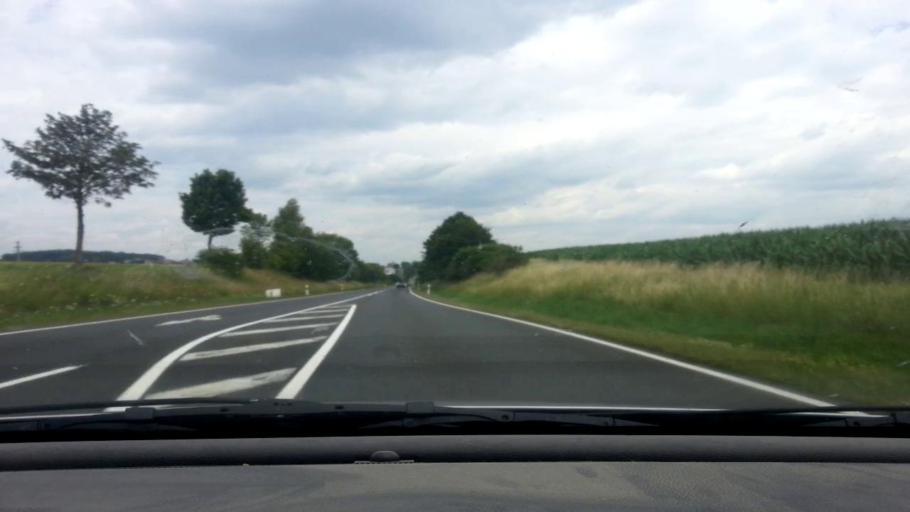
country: DE
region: Bavaria
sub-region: Upper Palatinate
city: Mitterteich
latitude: 49.9685
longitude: 12.2612
